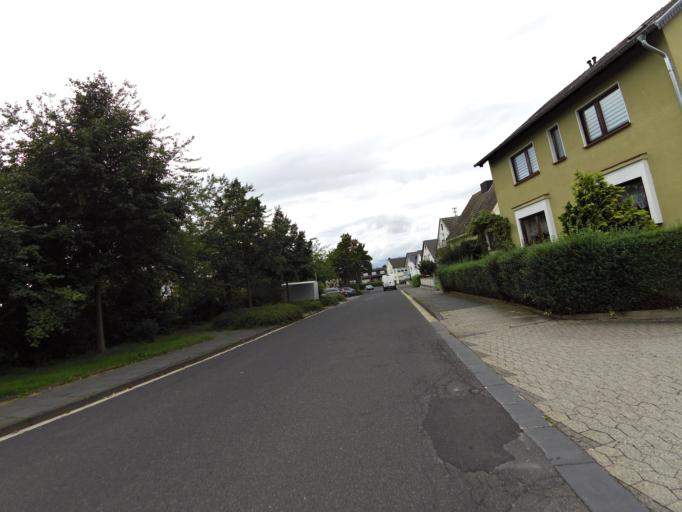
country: DE
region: North Rhine-Westphalia
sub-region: Regierungsbezirk Koln
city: Rheinbach
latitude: 50.6029
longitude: 6.9865
